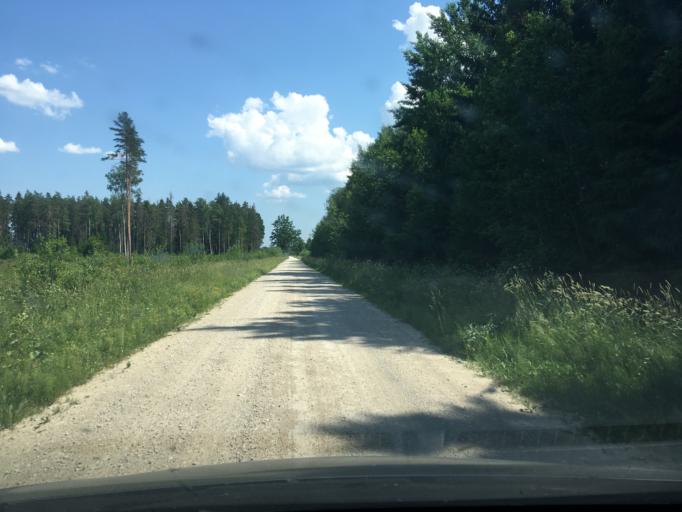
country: EE
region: Raplamaa
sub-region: Maerjamaa vald
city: Marjamaa
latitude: 58.8094
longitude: 24.4517
